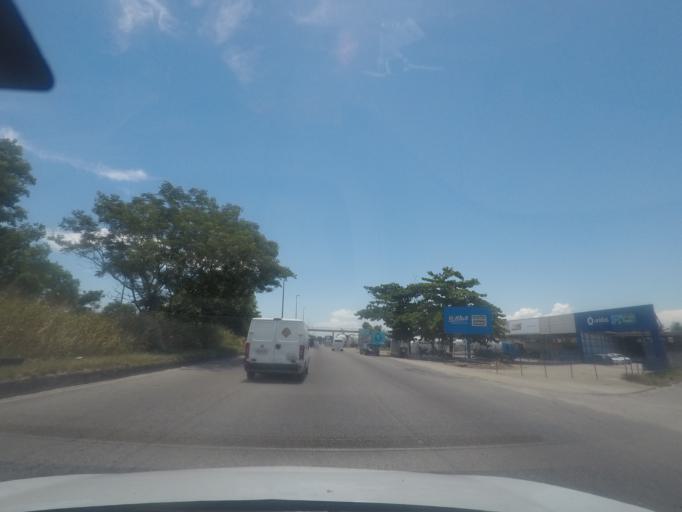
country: BR
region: Rio de Janeiro
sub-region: Itaguai
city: Itaguai
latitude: -22.8911
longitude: -43.6676
